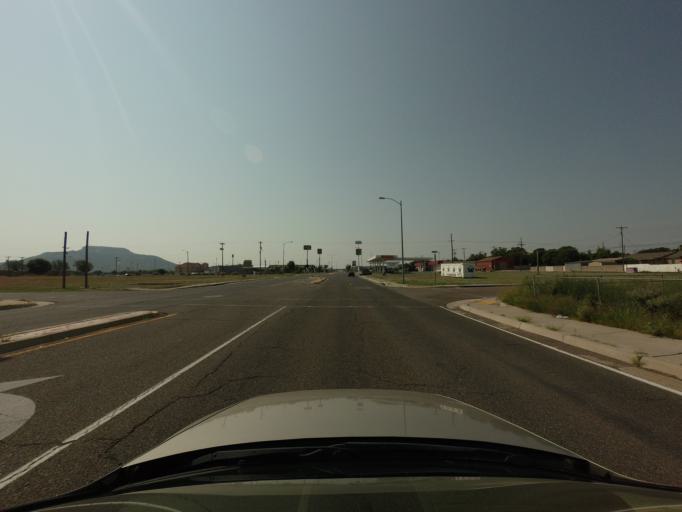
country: US
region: New Mexico
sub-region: Quay County
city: Tucumcari
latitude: 35.1581
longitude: -103.7251
